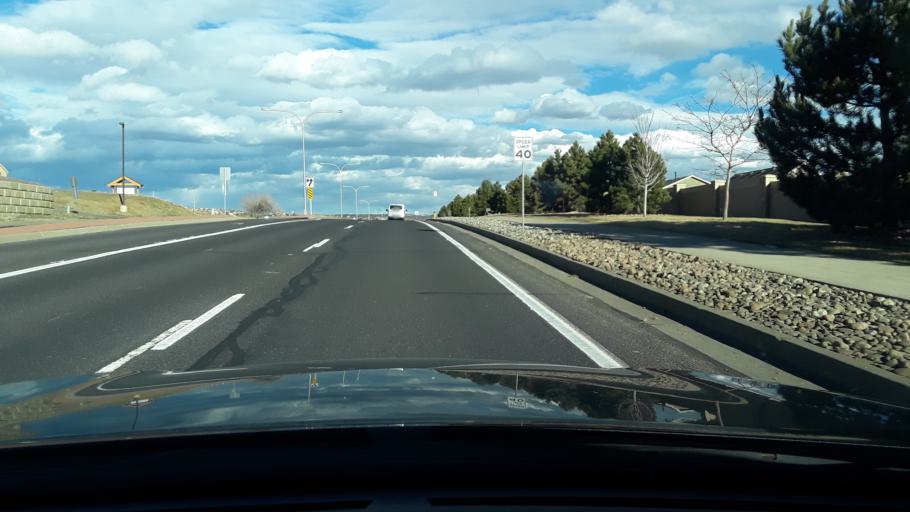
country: US
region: Colorado
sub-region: El Paso County
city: Gleneagle
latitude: 39.0272
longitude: -104.8113
